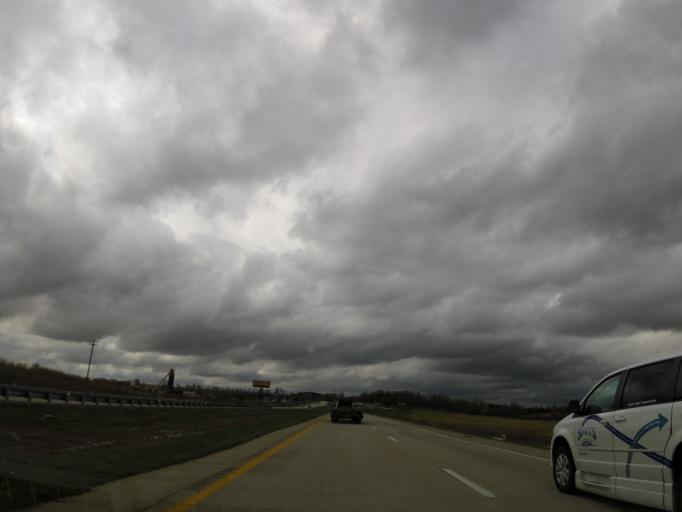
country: US
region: Missouri
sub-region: Butler County
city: Poplar Bluff
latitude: 36.6910
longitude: -90.4818
